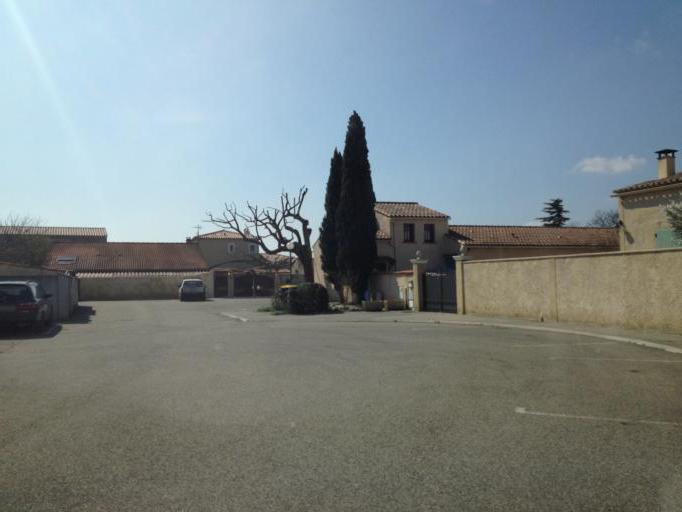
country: FR
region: Provence-Alpes-Cote d'Azur
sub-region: Departement du Vaucluse
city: Jonquieres
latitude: 44.1199
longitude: 4.9105
